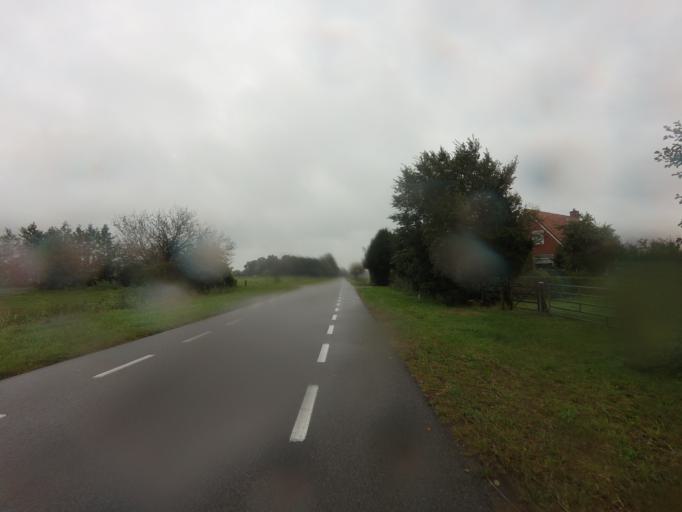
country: NL
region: Friesland
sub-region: Gemeente Smallingerland
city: Oudega
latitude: 53.0963
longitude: 5.9740
